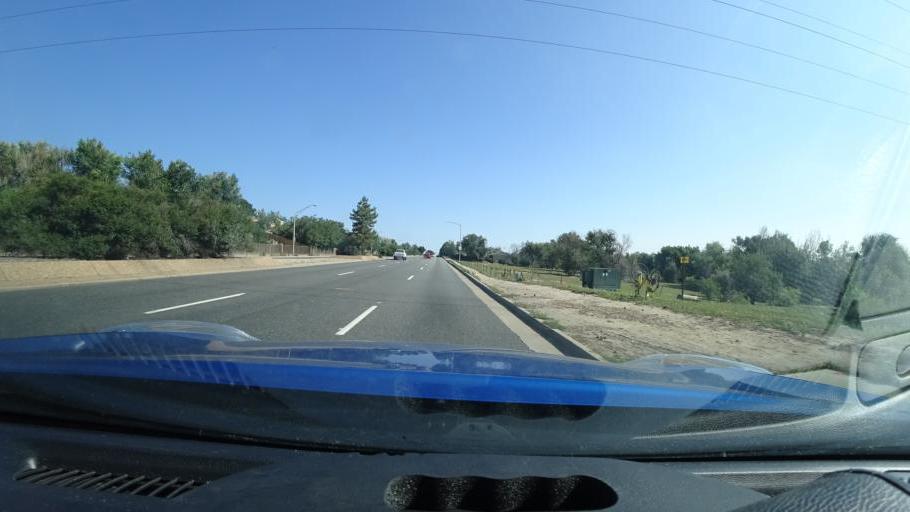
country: US
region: Colorado
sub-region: Adams County
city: Aurora
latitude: 39.6820
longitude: -104.8098
